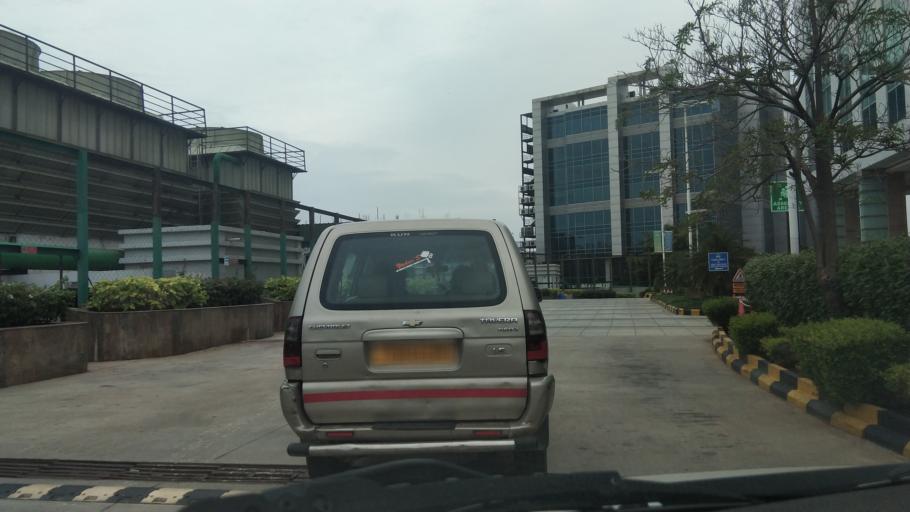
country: IN
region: Telangana
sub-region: Rangareddi
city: Kukatpalli
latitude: 17.4466
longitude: 78.3565
